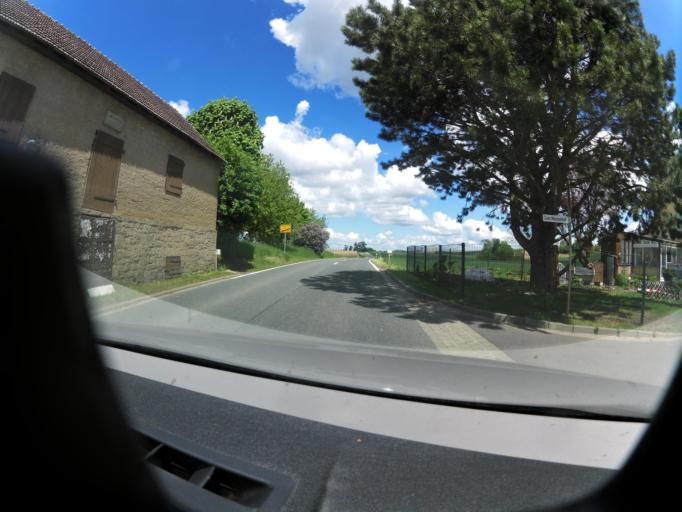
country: DE
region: Bavaria
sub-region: Regierungsbezirk Unterfranken
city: Prosselsheim
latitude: 49.8802
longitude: 10.1207
